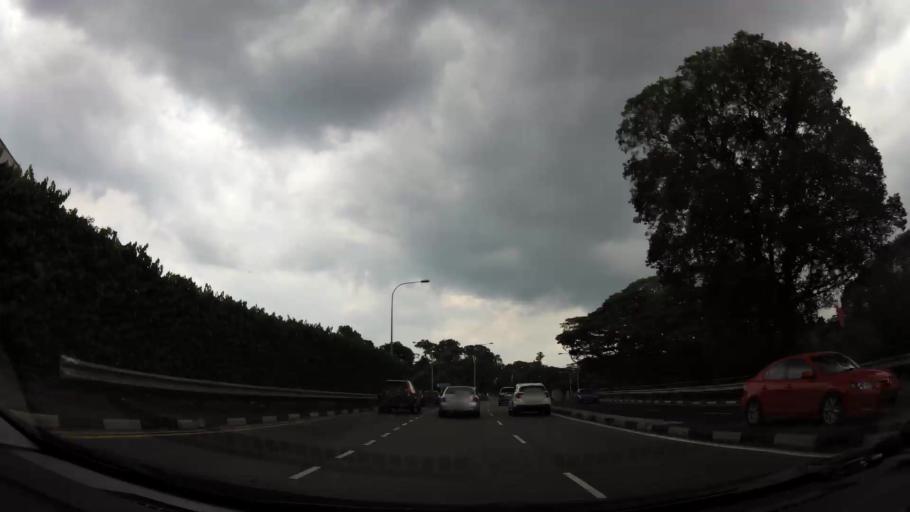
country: SG
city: Singapore
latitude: 1.3256
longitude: 103.8266
